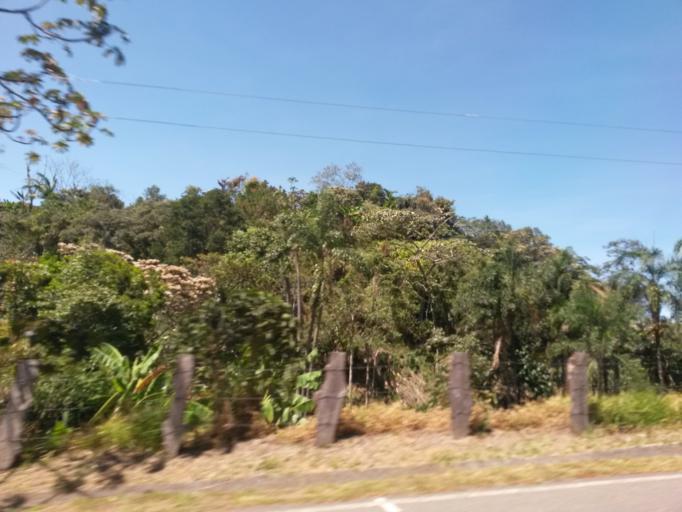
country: CO
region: Cauca
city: Lopez
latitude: 2.4408
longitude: -76.7805
